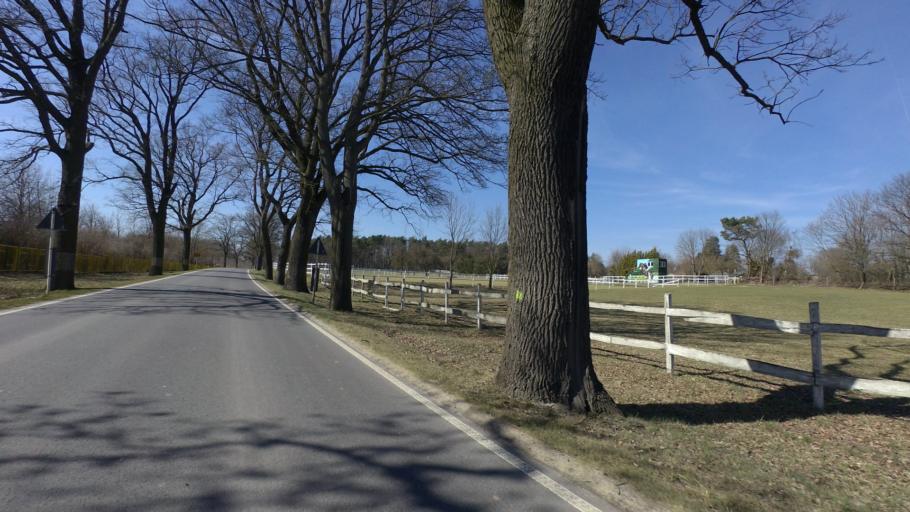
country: DE
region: Brandenburg
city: Waldsieversdorf
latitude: 52.5244
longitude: 14.0921
